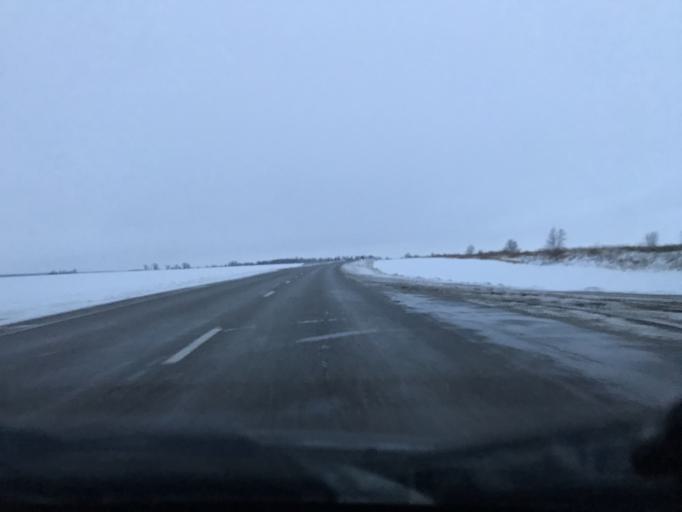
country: RU
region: Rostov
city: Letnik
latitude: 45.9522
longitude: 41.2824
